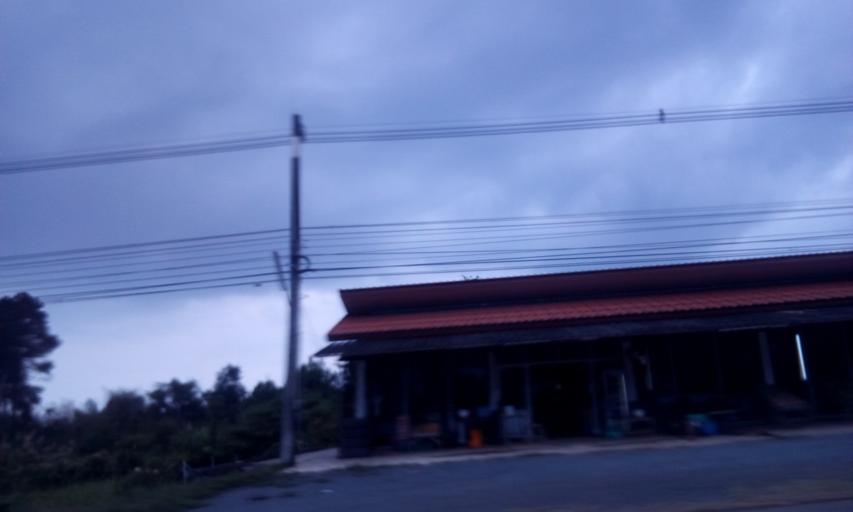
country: TH
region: Chanthaburi
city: Khlung
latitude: 12.4554
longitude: 102.2750
